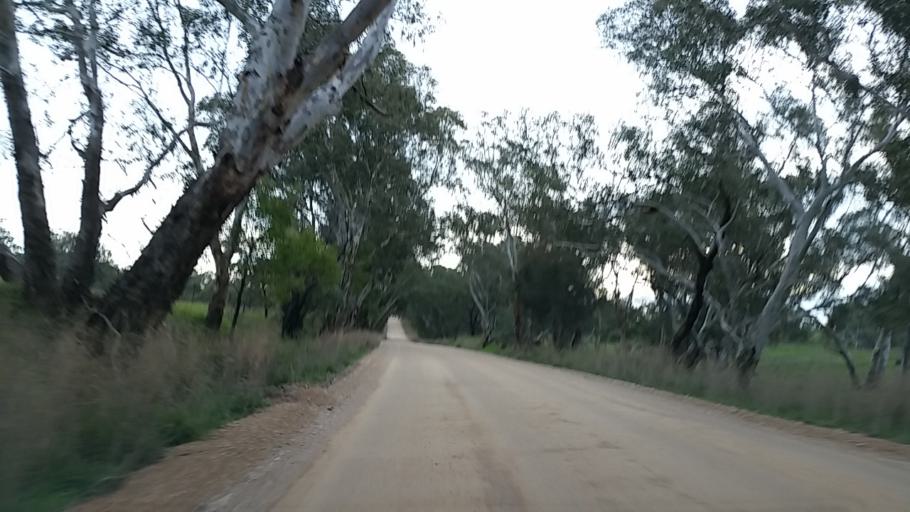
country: AU
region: South Australia
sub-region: Adelaide Hills
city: Birdwood
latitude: -34.8812
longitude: 139.0016
